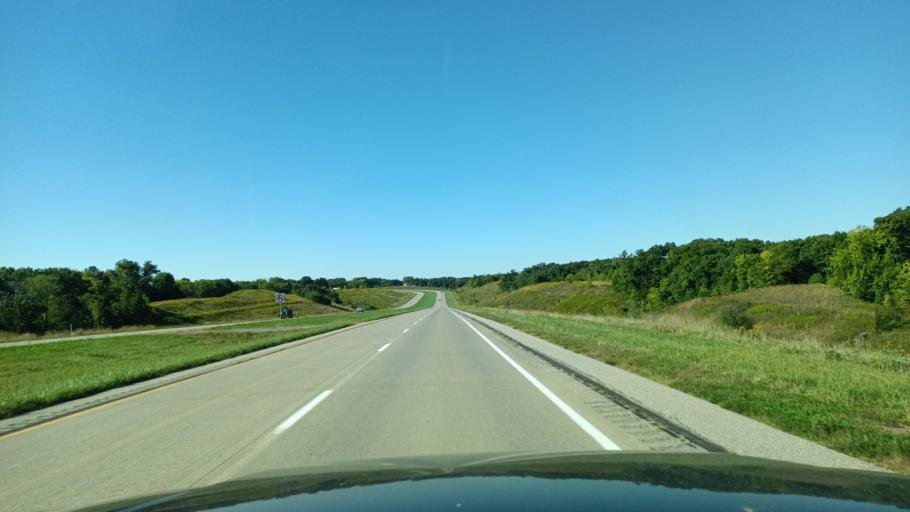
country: US
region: Iowa
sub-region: Lee County
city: Fort Madison
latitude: 40.6489
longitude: -91.3679
